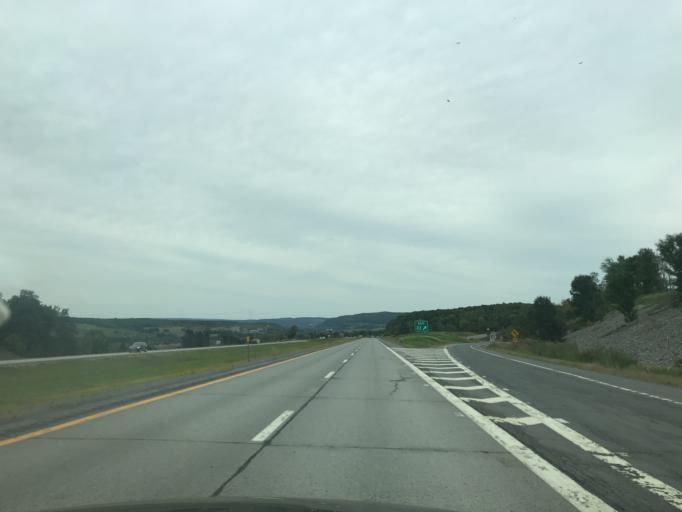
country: US
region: New York
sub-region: Schoharie County
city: Cobleskill
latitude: 42.6778
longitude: -74.4228
